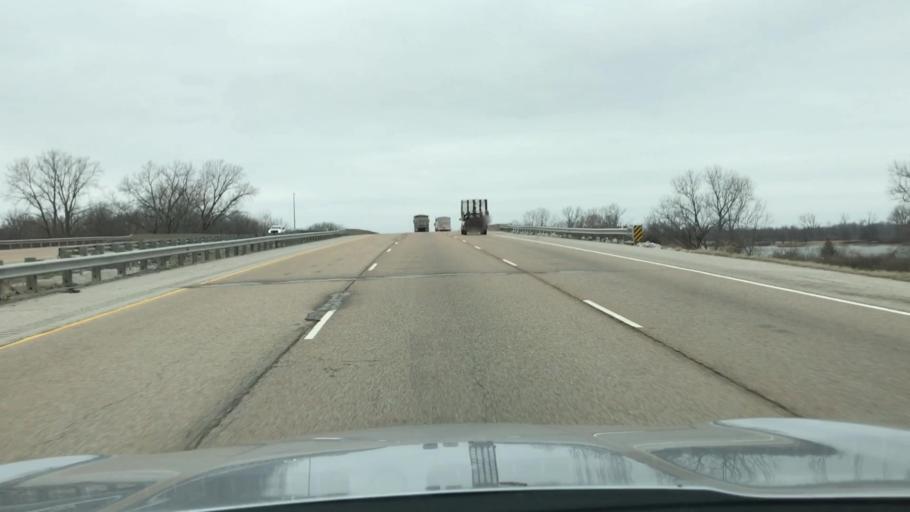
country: US
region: Illinois
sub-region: Saint Clair County
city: Fairmont City
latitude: 38.6628
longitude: -90.0784
